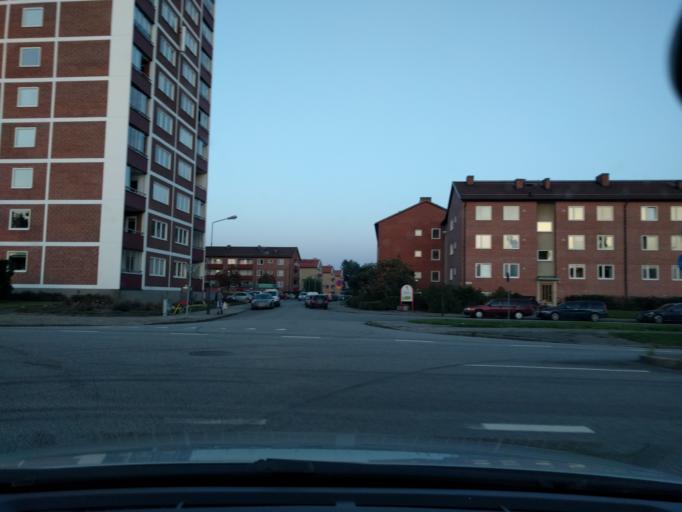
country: SE
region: Skane
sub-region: Malmo
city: Malmoe
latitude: 55.6002
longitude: 13.0390
